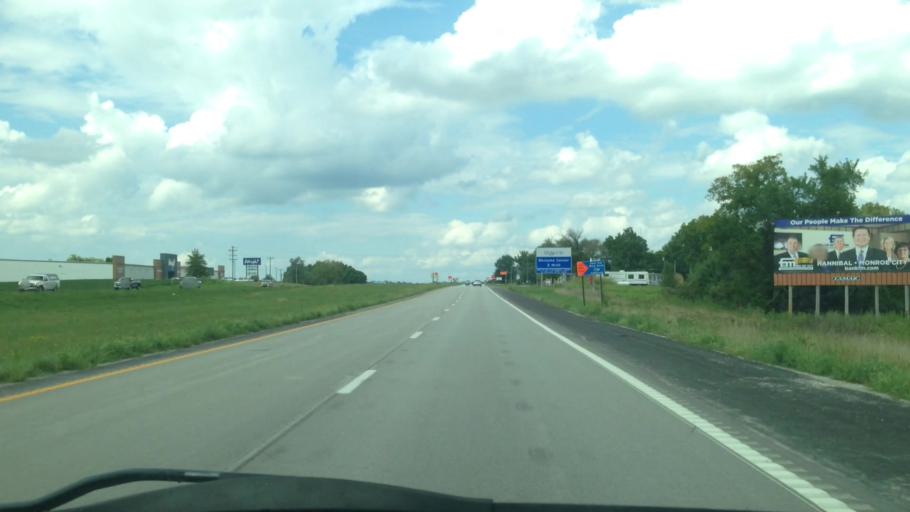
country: US
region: Missouri
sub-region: Marion County
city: Hannibal
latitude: 39.6613
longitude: -91.4181
